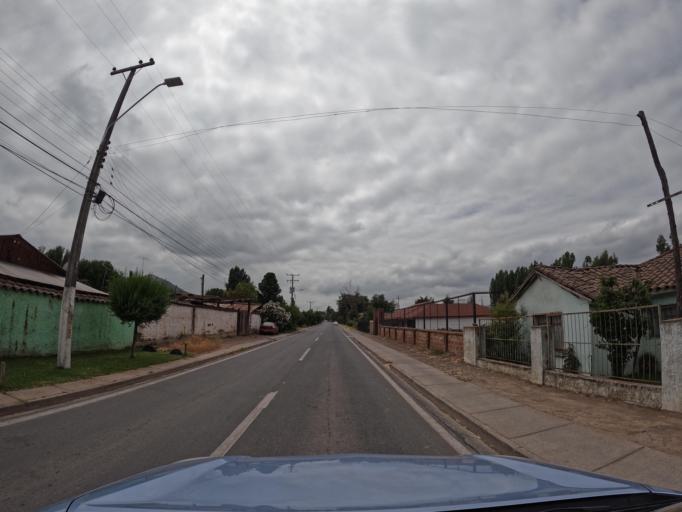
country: CL
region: Maule
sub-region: Provincia de Curico
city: Teno
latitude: -34.7608
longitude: -71.2003
